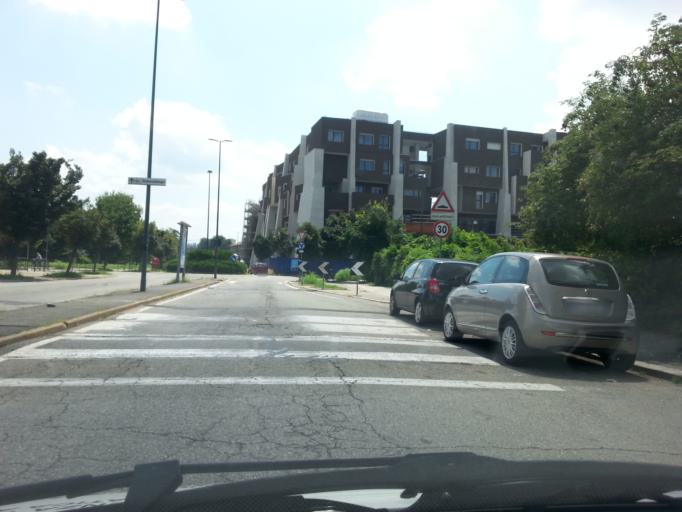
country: IT
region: Piedmont
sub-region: Provincia di Torino
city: Turin
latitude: 45.1030
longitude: 7.6847
